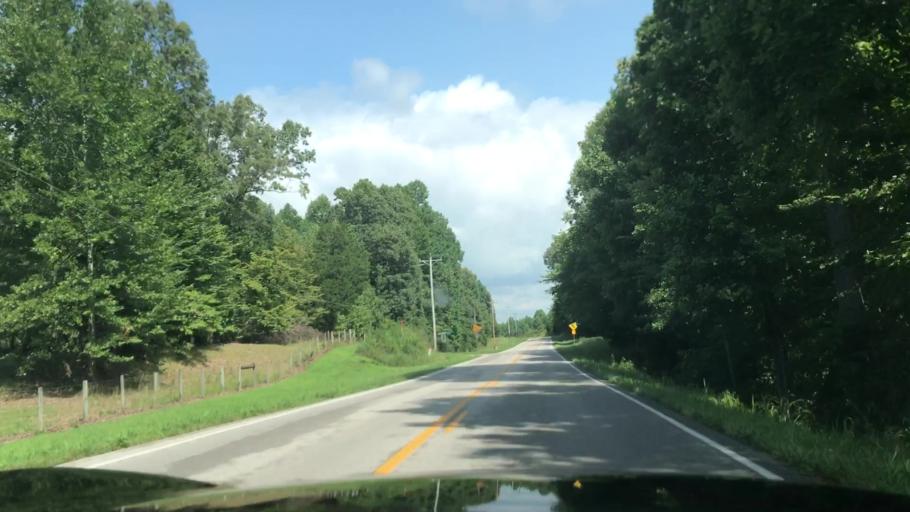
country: US
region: Kentucky
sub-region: Butler County
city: Morgantown
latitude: 37.1865
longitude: -86.8774
